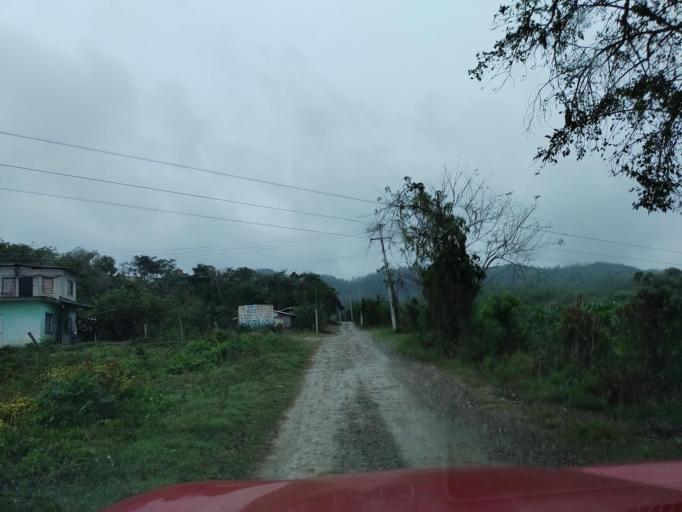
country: MX
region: Veracruz
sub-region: Papantla
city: El Chote
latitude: 20.3957
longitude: -97.3143
